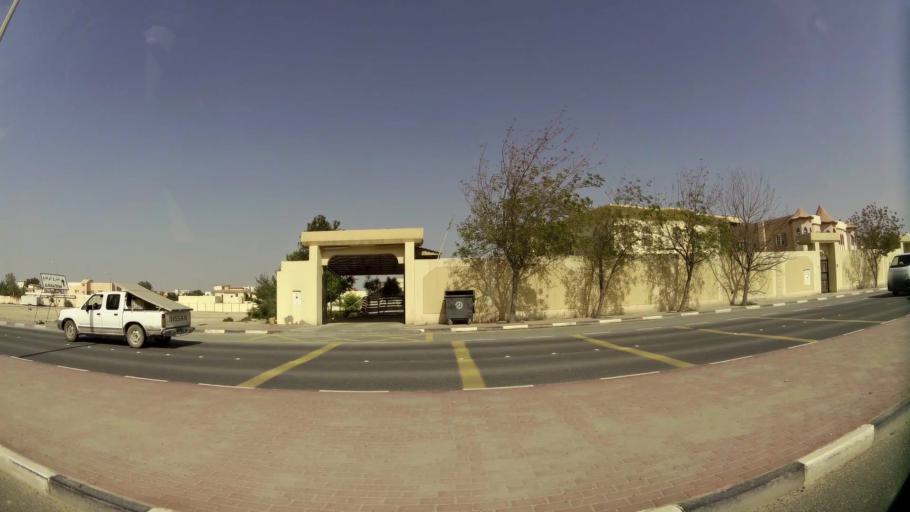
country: QA
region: Baladiyat Umm Salal
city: Umm Salal Muhammad
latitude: 25.3694
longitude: 51.4351
